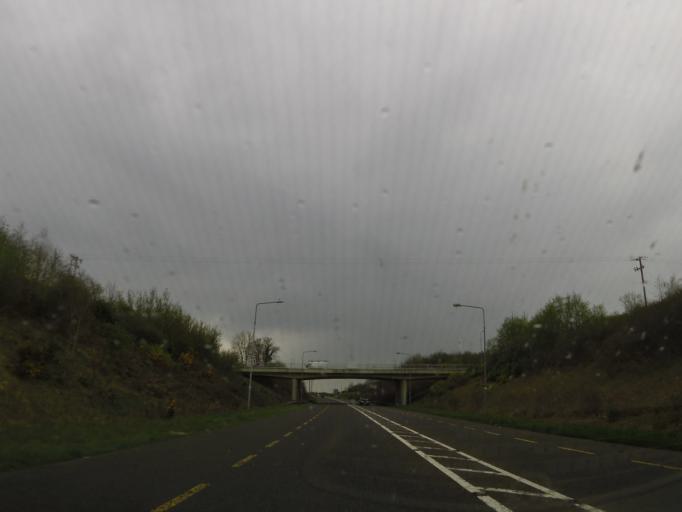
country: IE
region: Connaught
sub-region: Maigh Eo
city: Claremorris
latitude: 53.7251
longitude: -8.9829
